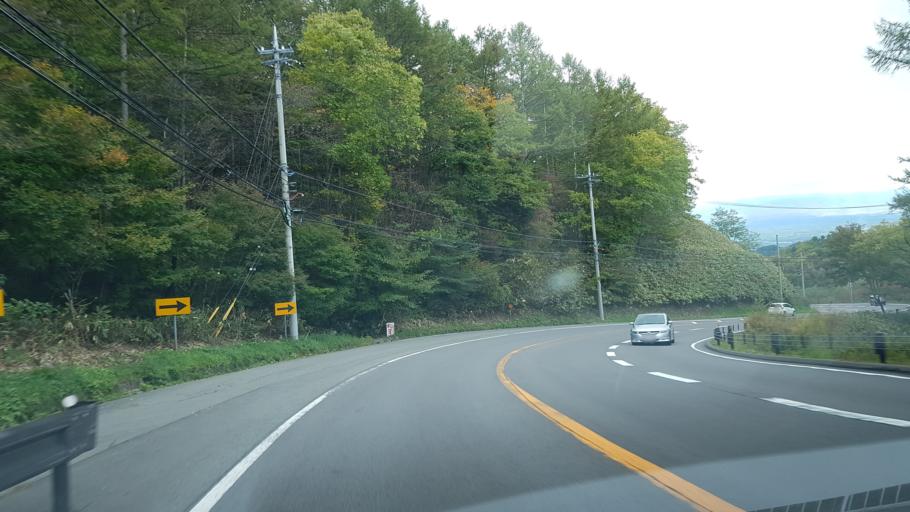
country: JP
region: Gunma
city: Nakanojomachi
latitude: 36.6002
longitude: 138.5871
